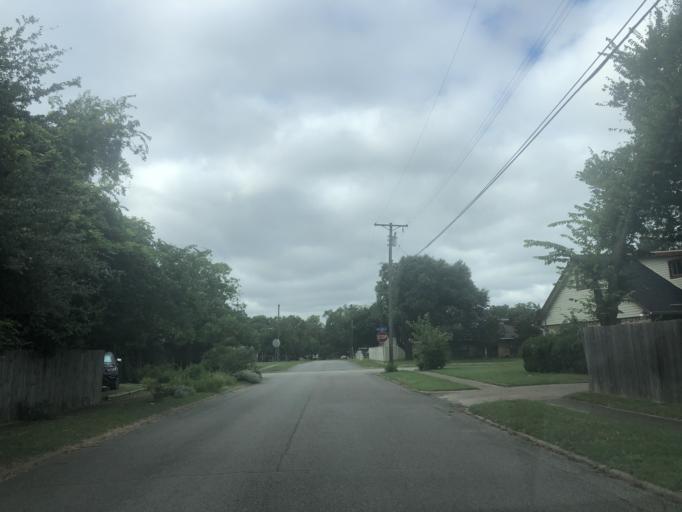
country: US
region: Texas
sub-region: Dallas County
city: Duncanville
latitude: 32.6550
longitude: -96.9129
